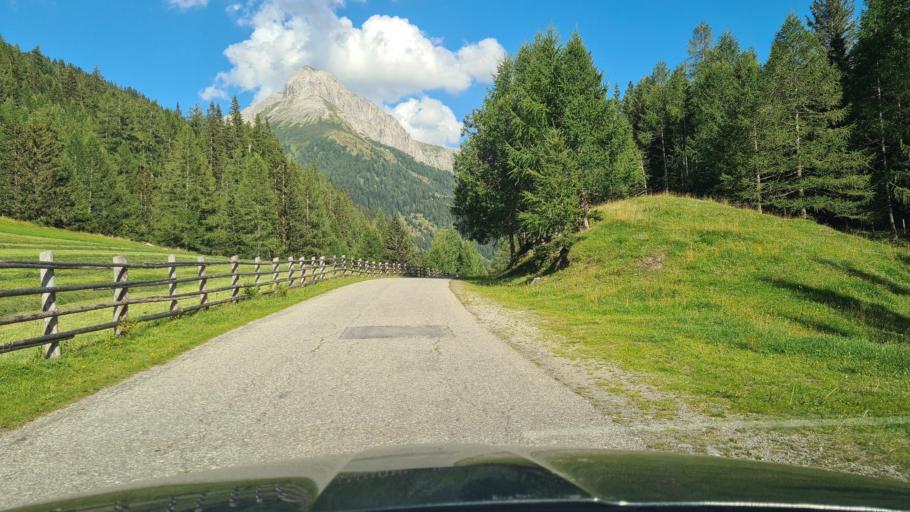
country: AT
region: Salzburg
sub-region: Politischer Bezirk Tamsweg
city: Zederhaus
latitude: 47.1859
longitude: 13.4203
